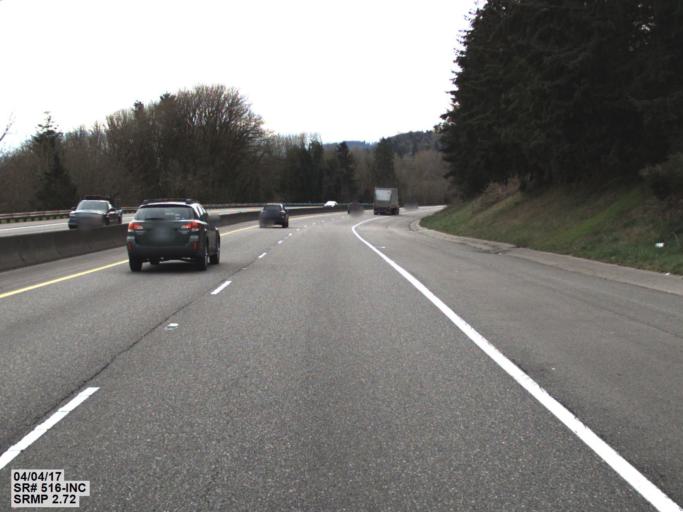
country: US
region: Washington
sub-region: King County
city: Kent
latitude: 47.3887
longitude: -122.2784
